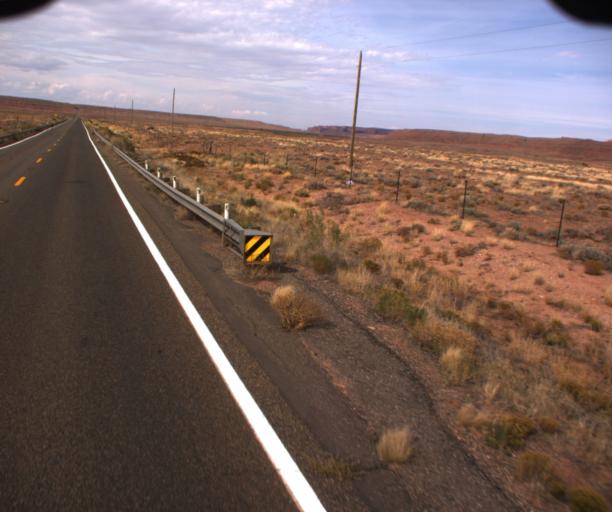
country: US
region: Arizona
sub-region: Apache County
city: Many Farms
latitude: 36.5217
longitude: -109.4928
